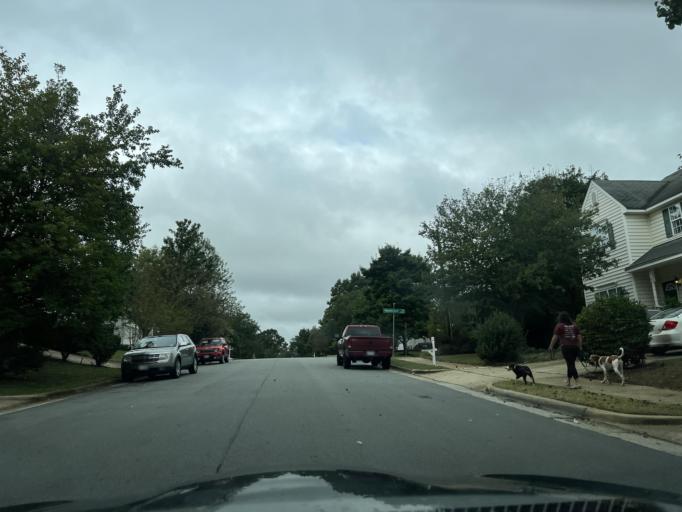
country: US
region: North Carolina
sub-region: Wake County
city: West Raleigh
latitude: 35.7471
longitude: -78.6827
